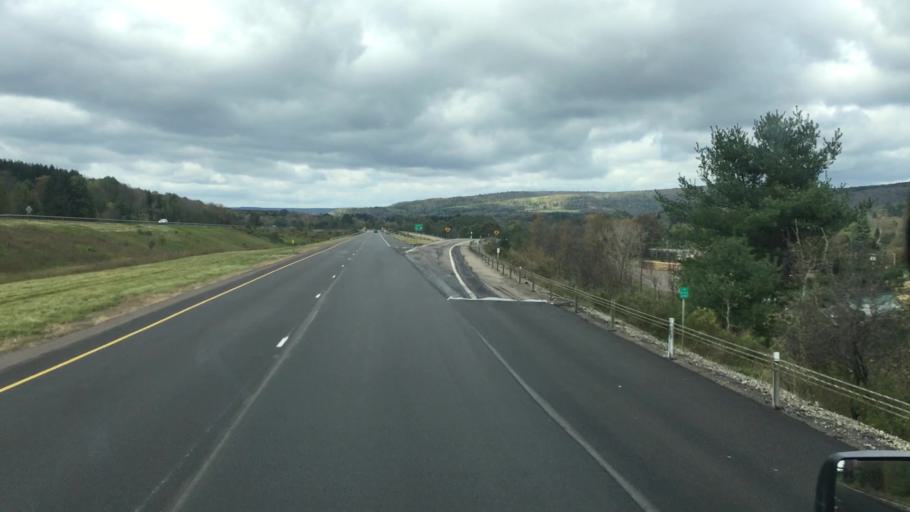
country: US
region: New York
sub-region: Allegany County
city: Belmont
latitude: 42.2991
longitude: -78.0063
